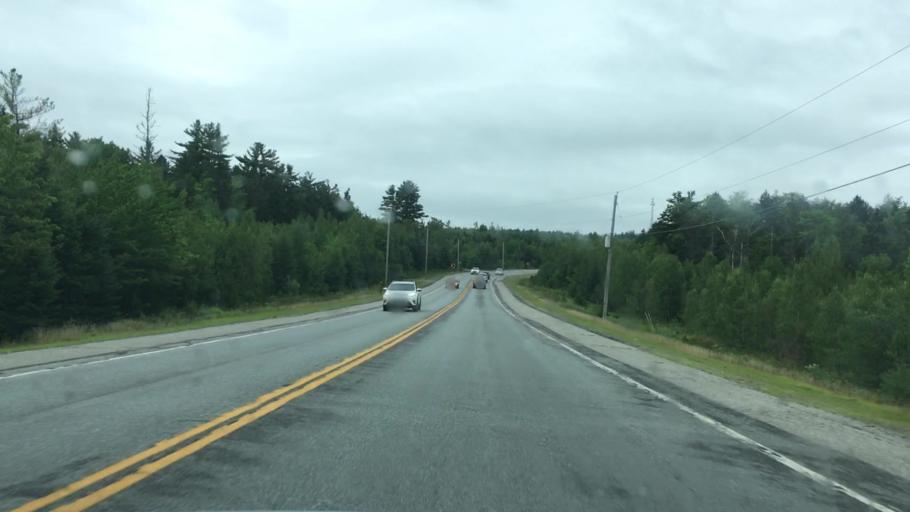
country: US
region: Maine
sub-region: Washington County
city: Cherryfield
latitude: 44.8507
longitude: -68.0603
